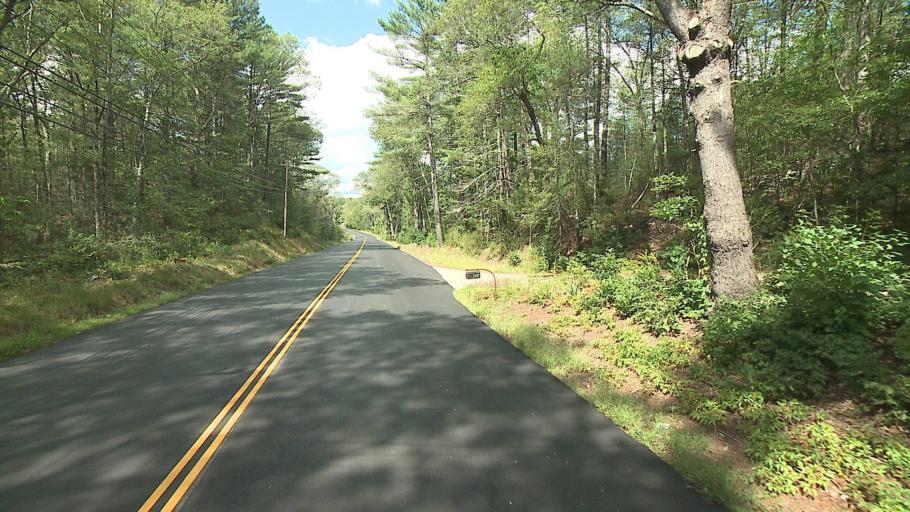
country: US
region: Connecticut
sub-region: Windham County
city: Thompson
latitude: 41.9253
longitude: -71.8513
